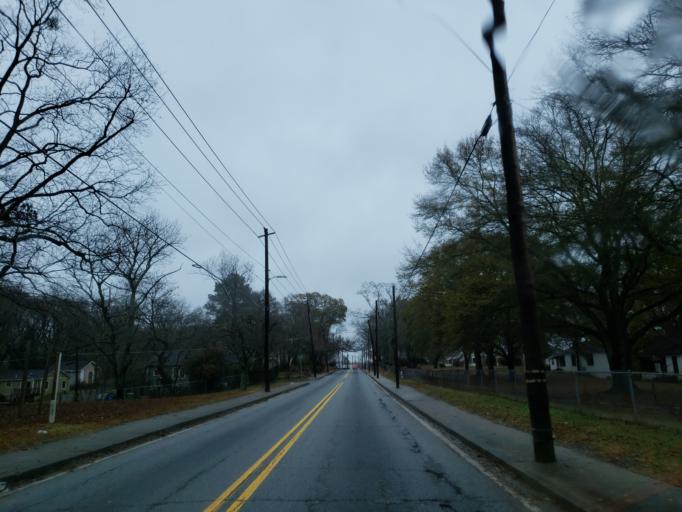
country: US
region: Georgia
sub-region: Fulton County
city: Atlanta
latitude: 33.7118
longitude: -84.3638
